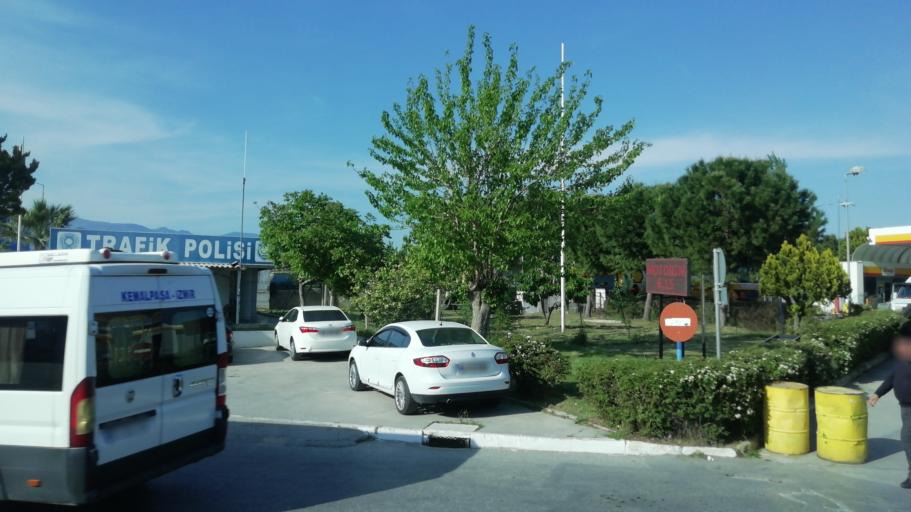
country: TR
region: Izmir
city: Bornova
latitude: 38.4324
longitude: 27.2127
